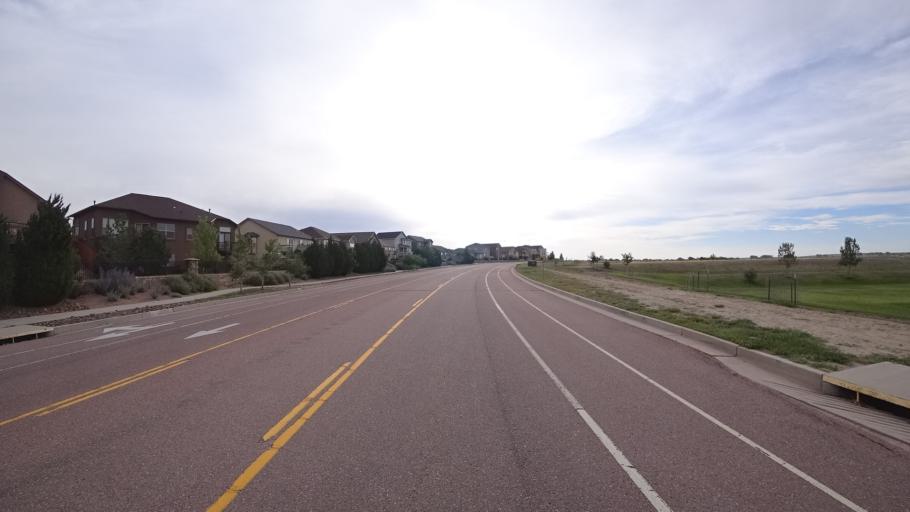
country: US
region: Colorado
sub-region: El Paso County
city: Fountain
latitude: 38.7153
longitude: -104.6855
